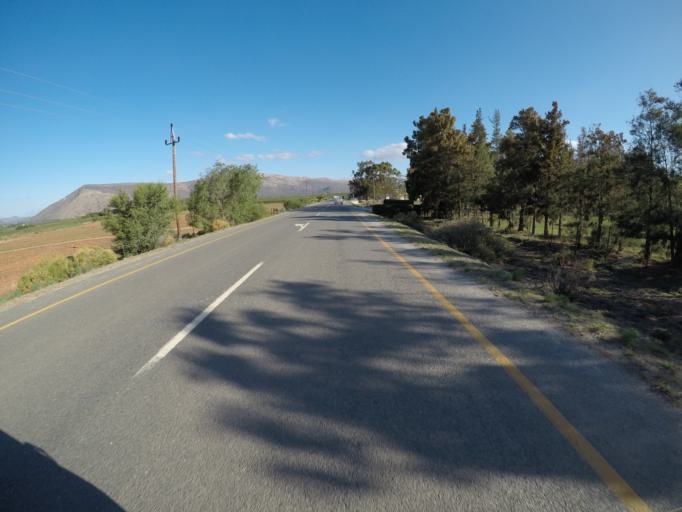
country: ZA
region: Western Cape
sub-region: Cape Winelands District Municipality
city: Ashton
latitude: -33.8094
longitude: 19.7824
